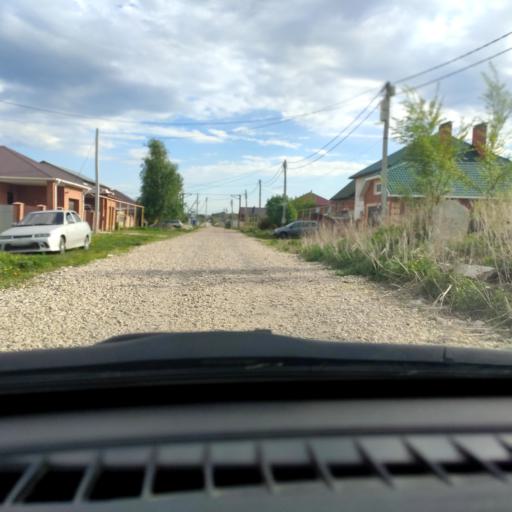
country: RU
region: Samara
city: Tol'yatti
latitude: 53.5672
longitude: 49.4080
